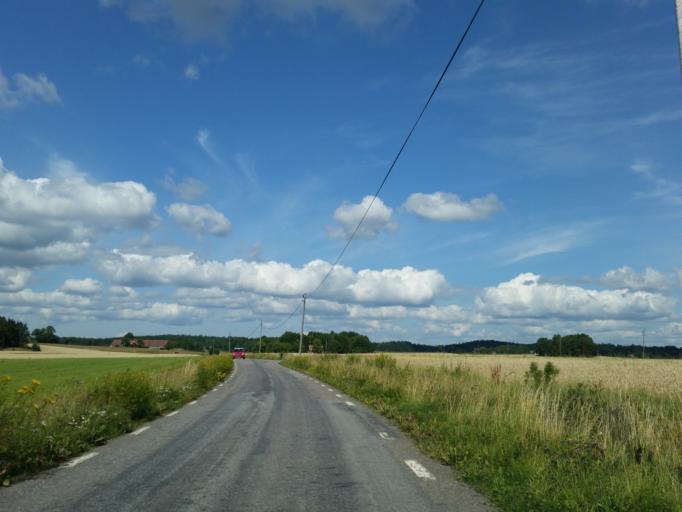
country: SE
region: Soedermanland
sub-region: Trosa Kommun
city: Trosa
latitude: 58.9847
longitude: 17.6558
